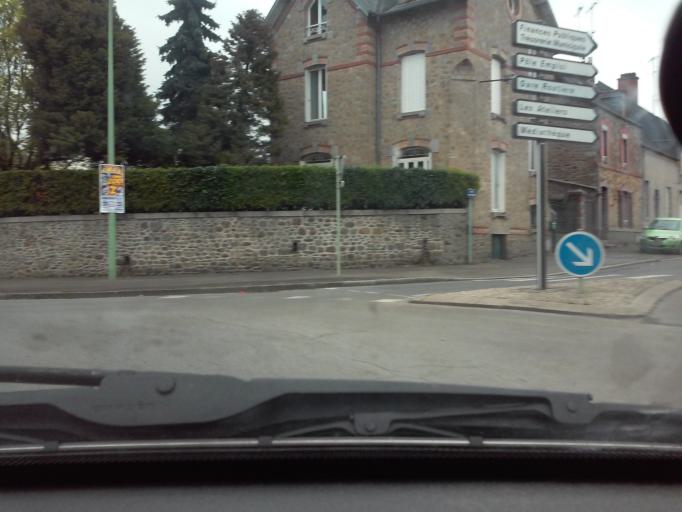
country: FR
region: Brittany
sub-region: Departement d'Ille-et-Vilaine
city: Fougeres
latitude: 48.3469
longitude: -1.1876
